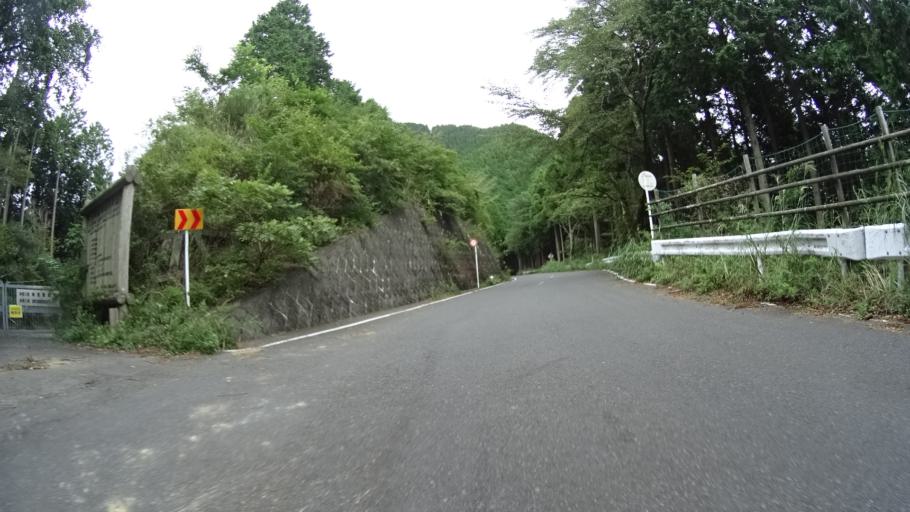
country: JP
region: Kanagawa
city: Hadano
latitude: 35.4200
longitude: 139.2140
